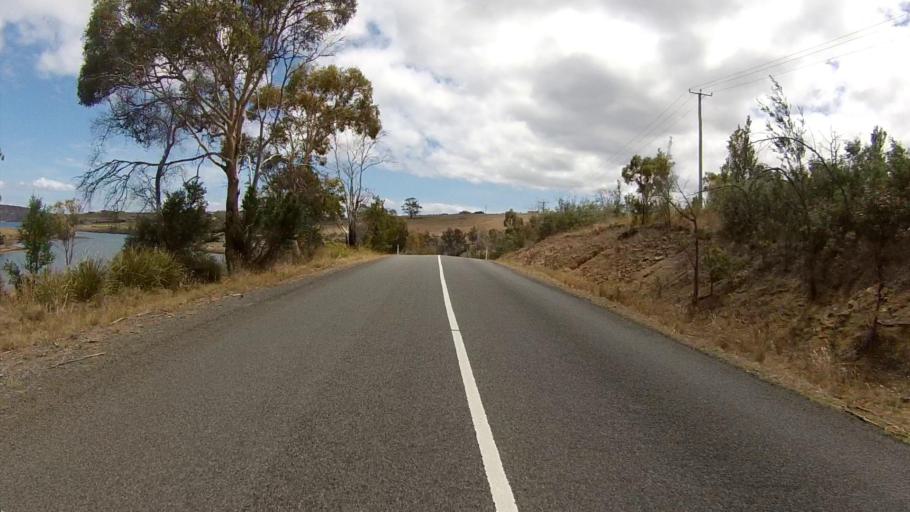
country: AU
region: Tasmania
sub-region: Sorell
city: Sorell
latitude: -42.8631
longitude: 147.6874
